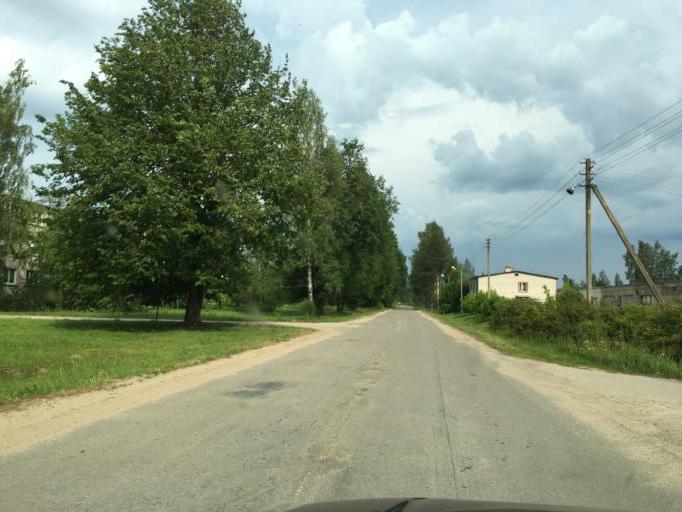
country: LV
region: Vilanu
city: Vilani
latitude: 56.6805
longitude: 26.9408
